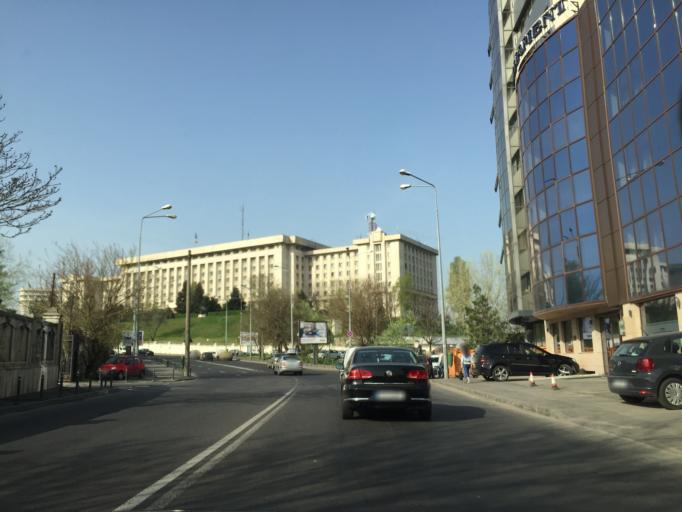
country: RO
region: Bucuresti
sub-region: Municipiul Bucuresti
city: Bucuresti
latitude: 44.4292
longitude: 26.0806
